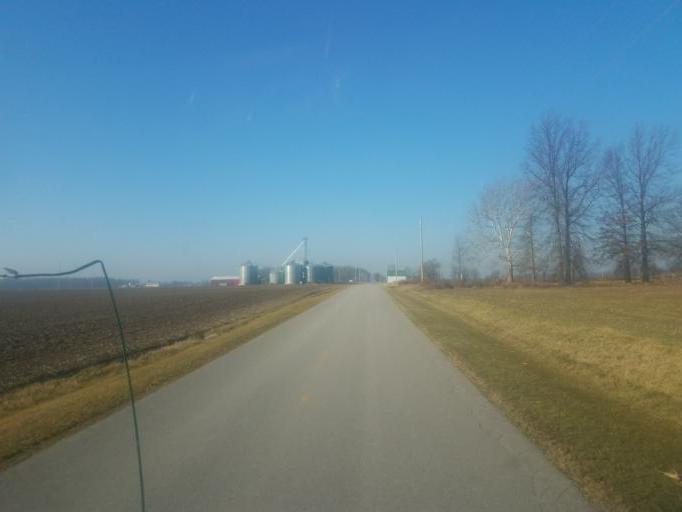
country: US
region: Ohio
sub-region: Seneca County
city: Tiffin
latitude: 41.0371
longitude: -82.9730
